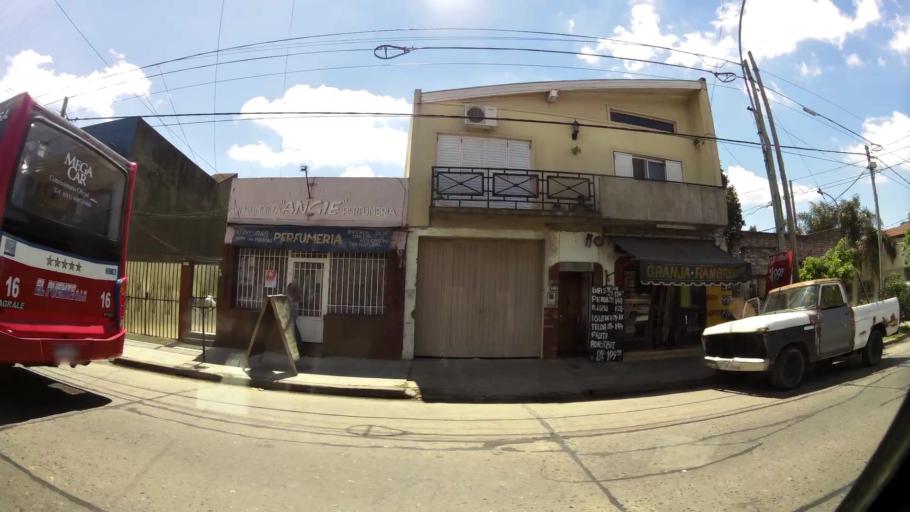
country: AR
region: Buenos Aires
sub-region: Partido de Lanus
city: Lanus
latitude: -34.6962
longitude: -58.4226
